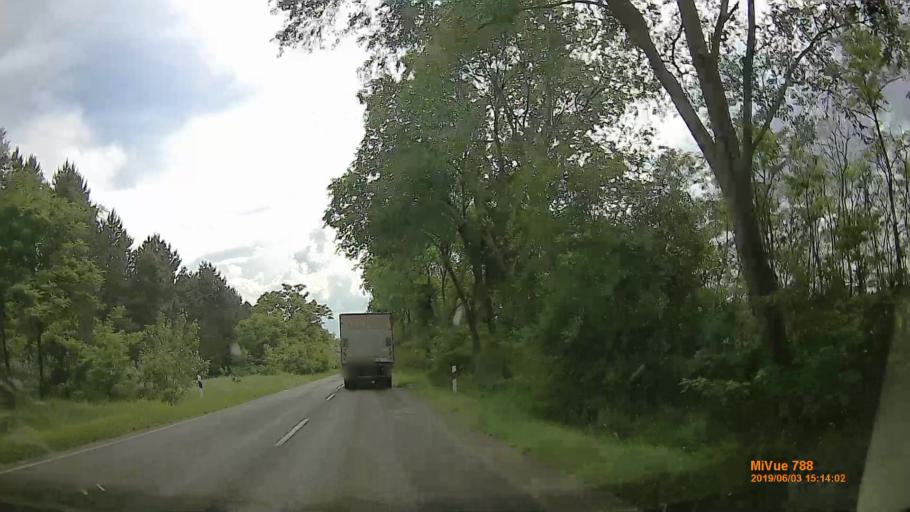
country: HU
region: Bacs-Kiskun
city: Orgovany
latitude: 46.7358
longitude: 19.5645
